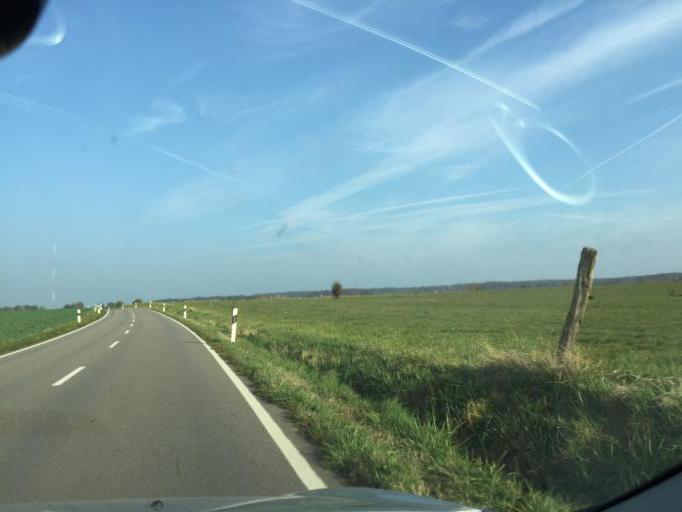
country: LU
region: Grevenmacher
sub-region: Canton de Remich
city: Dalheim
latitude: 49.5398
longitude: 6.2398
